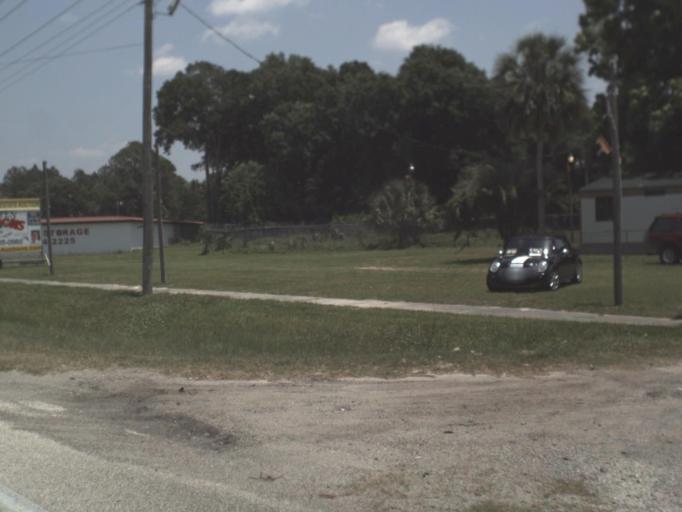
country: US
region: Florida
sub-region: Bradford County
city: Starke
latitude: 29.9295
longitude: -82.1207
